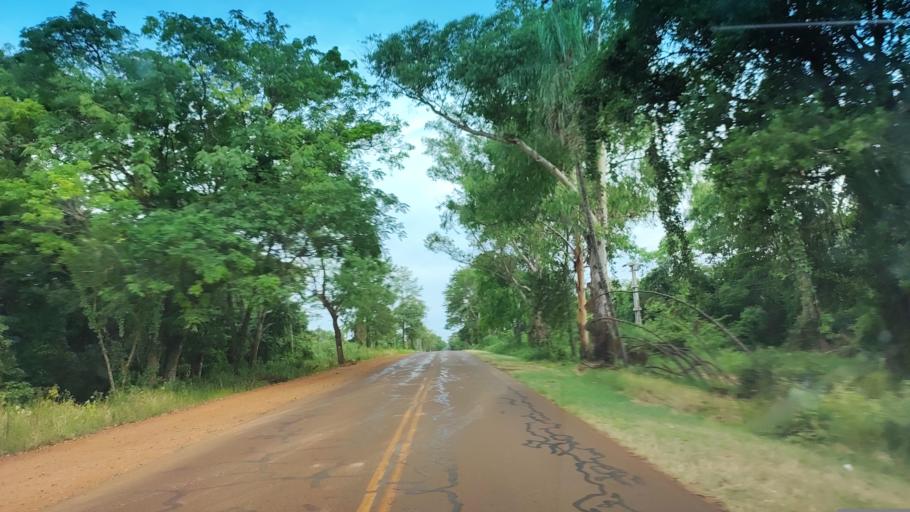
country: AR
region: Misiones
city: Gobernador Roca
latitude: -27.1437
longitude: -55.4949
